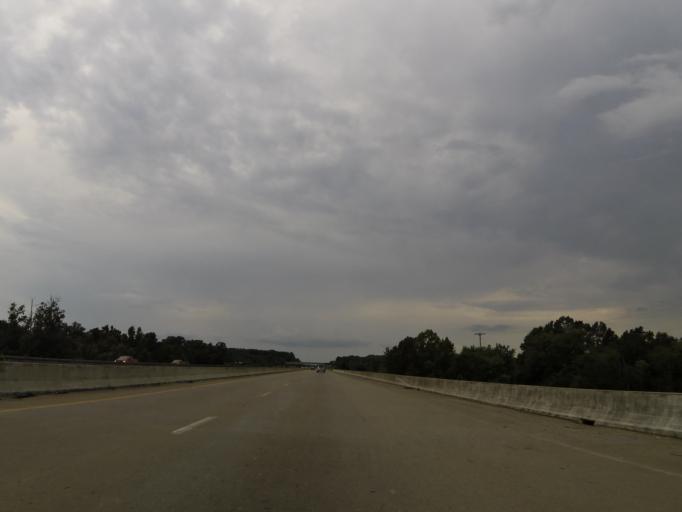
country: US
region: Tennessee
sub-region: Rutherford County
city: Smyrna
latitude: 35.9805
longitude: -86.4421
